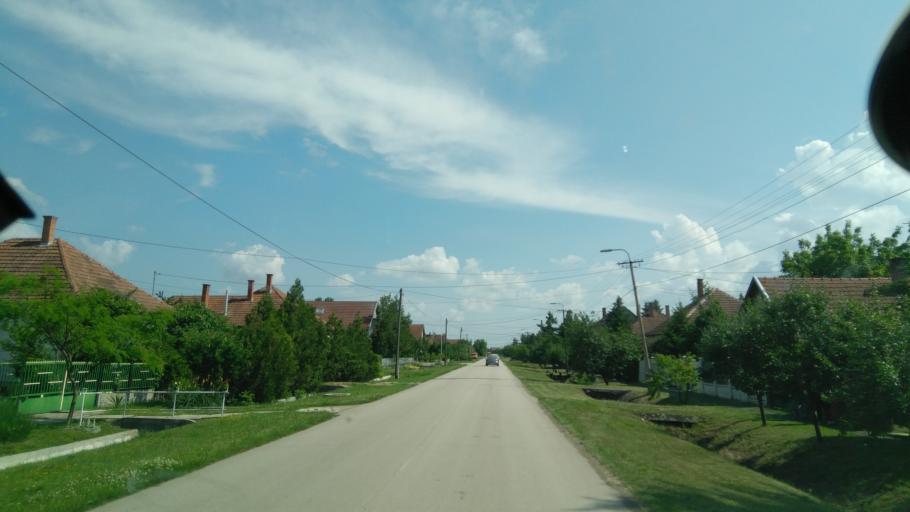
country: HU
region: Bekes
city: Doboz
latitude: 46.7389
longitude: 21.2362
